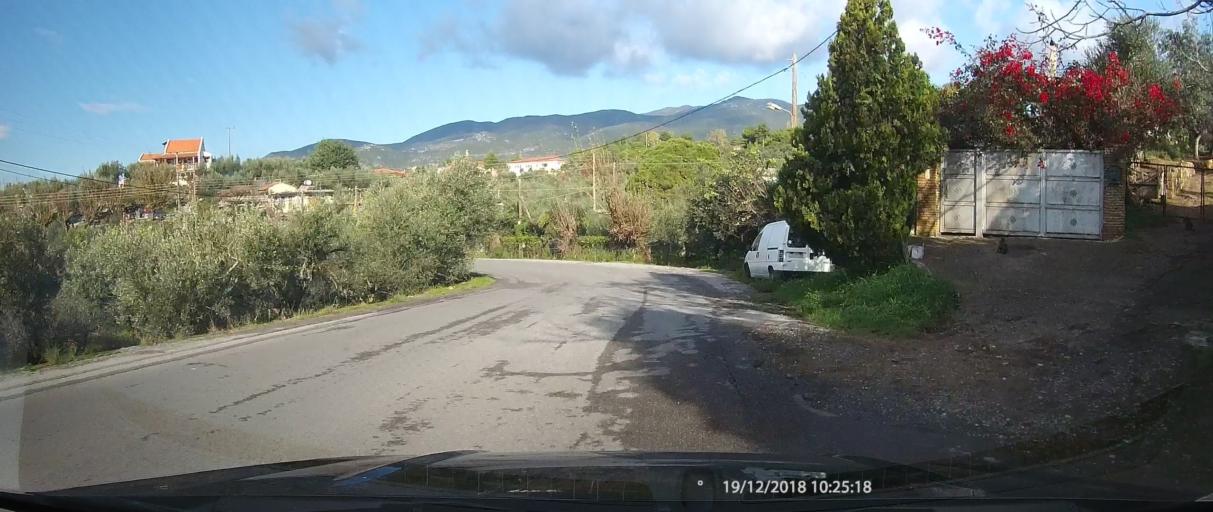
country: GR
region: Peloponnese
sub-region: Nomos Messinias
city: Kalamata
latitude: 37.0471
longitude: 22.1326
